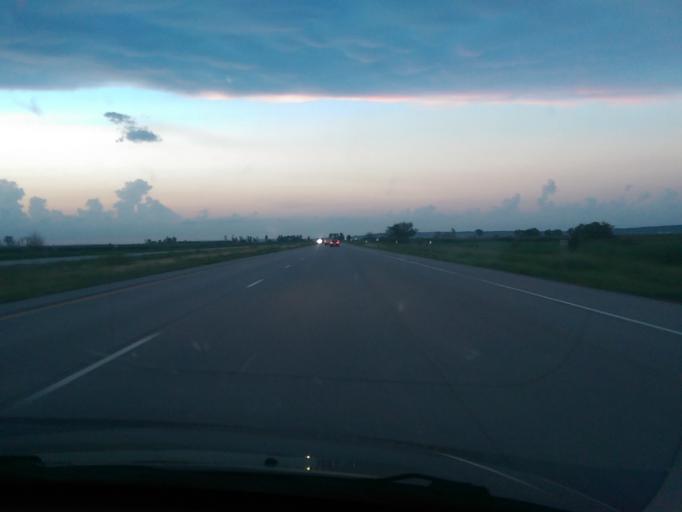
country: US
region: Nebraska
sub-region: Otoe County
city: Nebraska City
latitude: 40.7626
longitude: -95.8152
